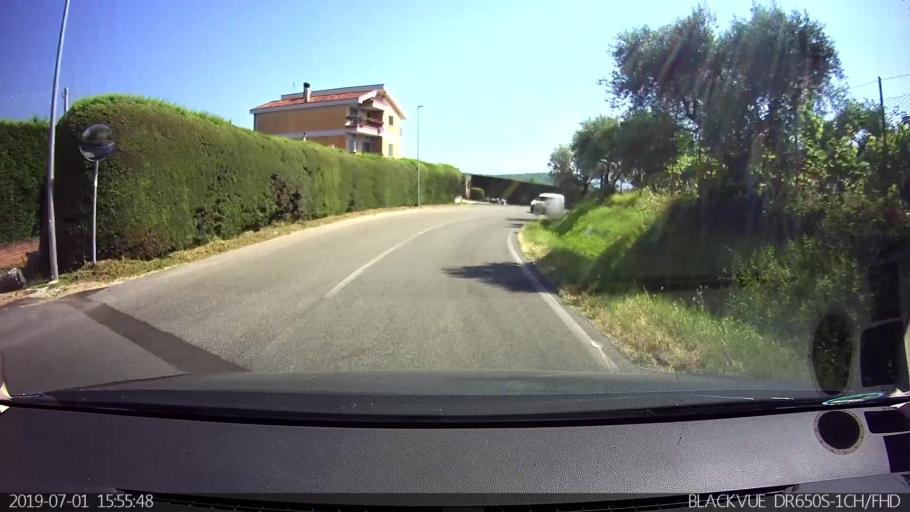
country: IT
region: Latium
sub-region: Provincia di Frosinone
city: Veroli
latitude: 41.6856
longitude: 13.4228
